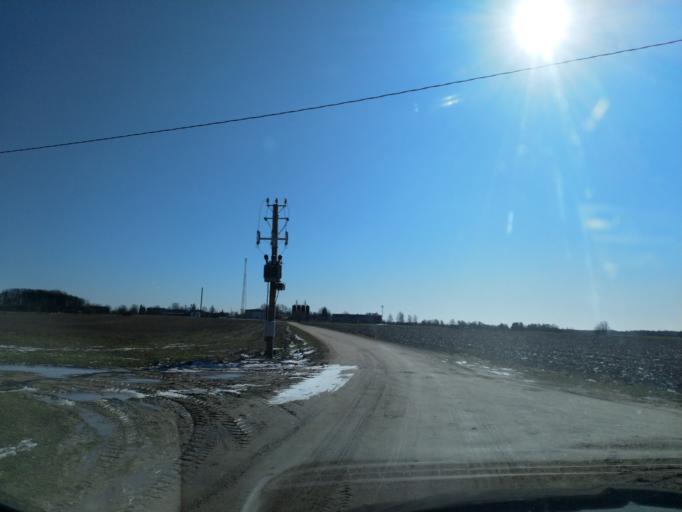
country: LV
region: Broceni
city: Broceni
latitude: 56.8346
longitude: 22.3956
